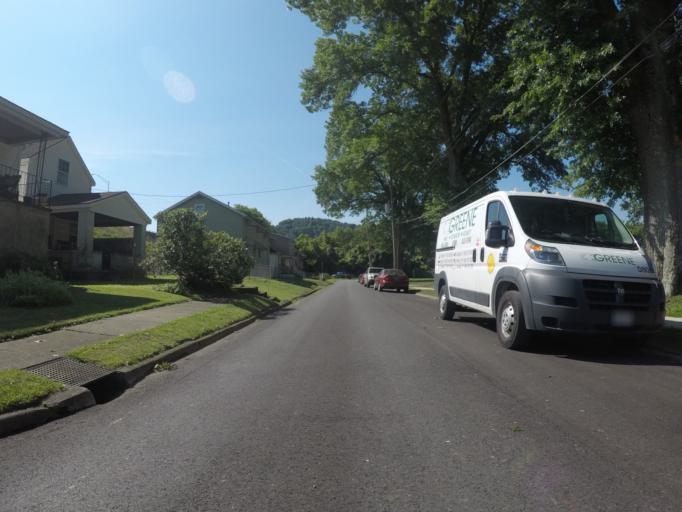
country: US
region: West Virginia
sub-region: Cabell County
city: Huntington
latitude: 38.4052
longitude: -82.4821
